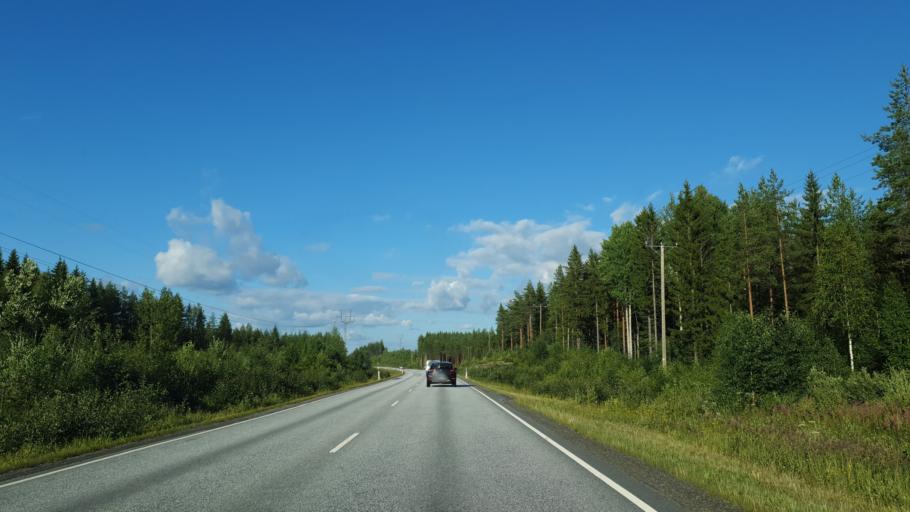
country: FI
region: North Karelia
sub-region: Joensuu
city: Outokumpu
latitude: 62.5353
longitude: 29.1074
